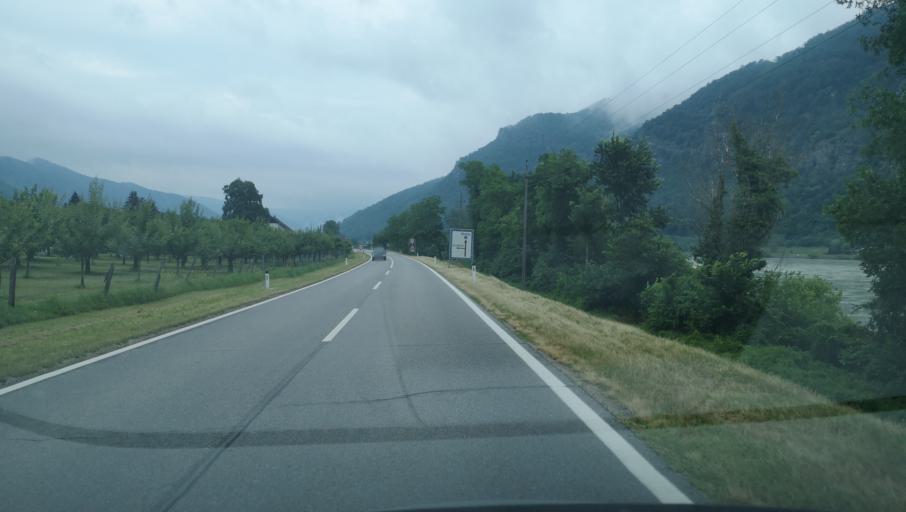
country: AT
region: Lower Austria
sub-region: Politischer Bezirk Krems
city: Aggsbach
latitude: 48.3132
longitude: 15.4079
